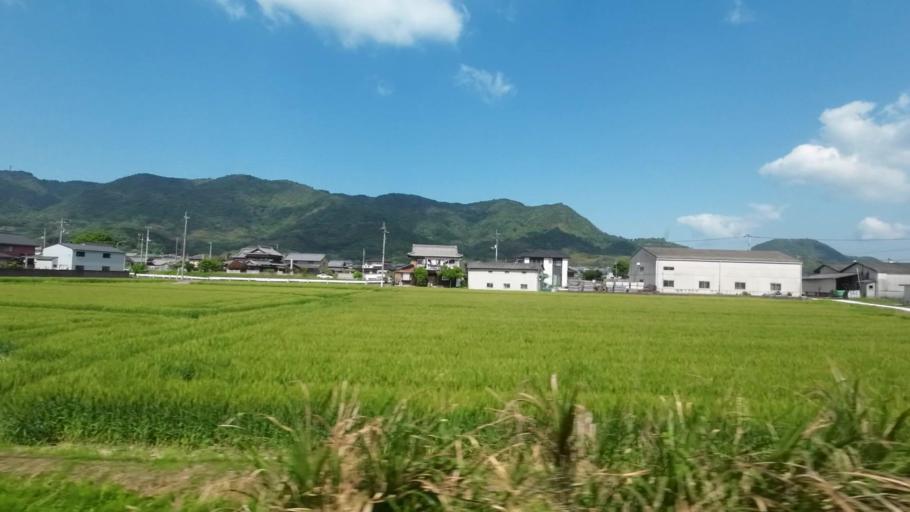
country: JP
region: Kagawa
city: Kan'onjicho
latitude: 34.1747
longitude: 133.6930
